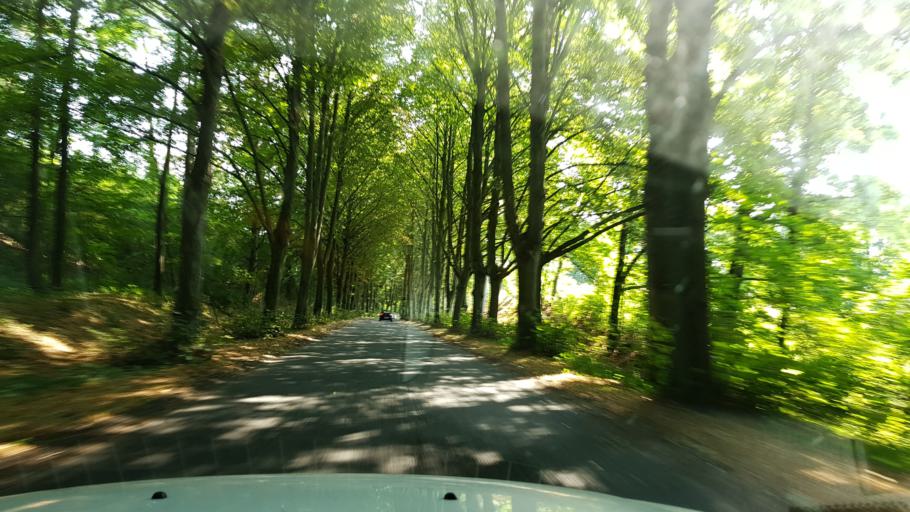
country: PL
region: West Pomeranian Voivodeship
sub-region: Powiat gryfinski
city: Chojna
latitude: 52.9586
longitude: 14.4851
